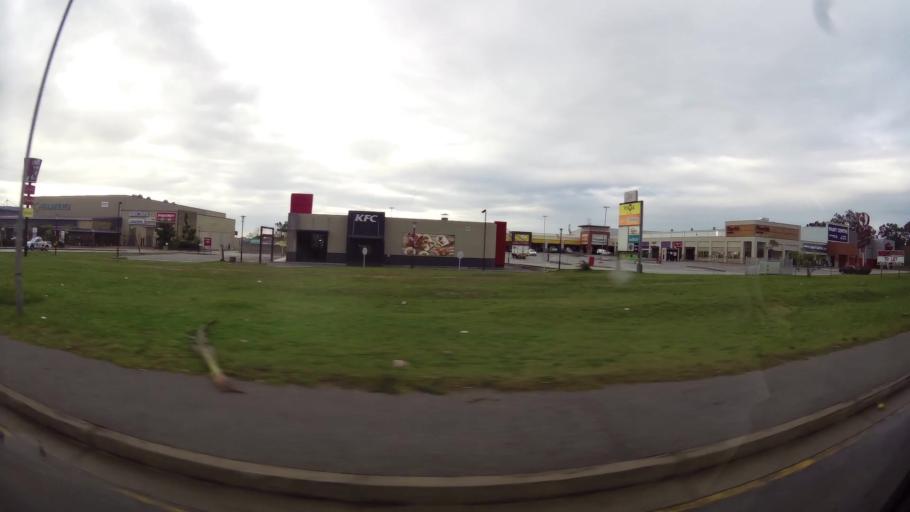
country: ZA
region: Eastern Cape
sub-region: Nelson Mandela Bay Metropolitan Municipality
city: Port Elizabeth
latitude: -33.9845
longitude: 25.5530
